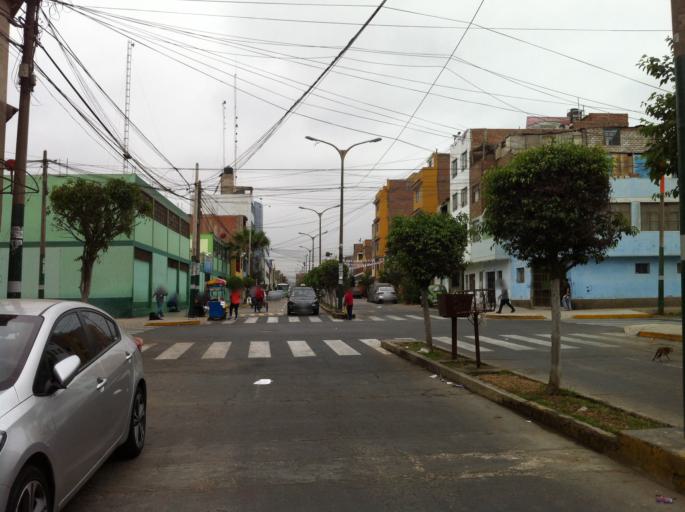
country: PE
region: Callao
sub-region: Callao
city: Callao
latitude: -12.0404
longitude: -77.0977
